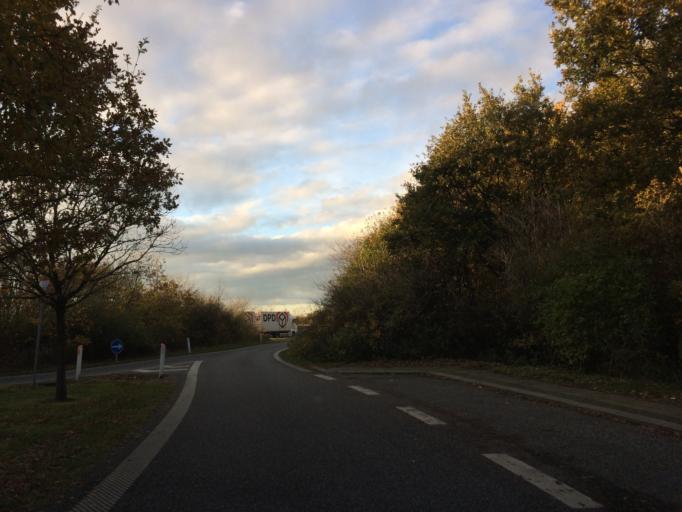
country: DK
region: South Denmark
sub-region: Aabenraa Kommune
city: Aabenraa
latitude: 55.0235
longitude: 9.3629
